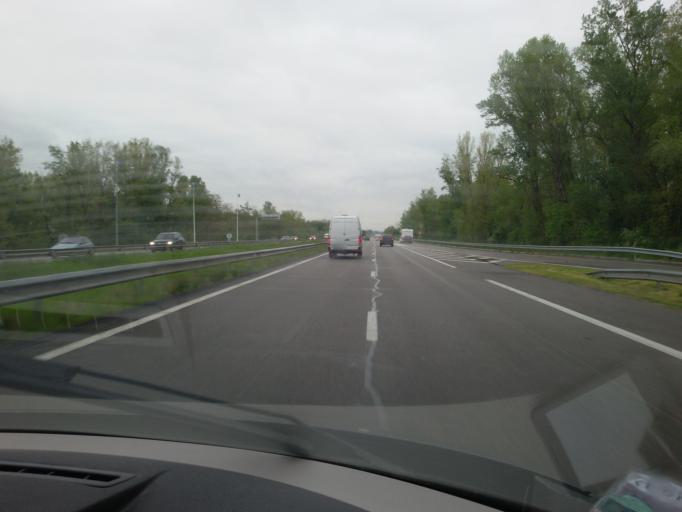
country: FR
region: Rhone-Alpes
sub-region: Departement du Rhone
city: Les Cheres
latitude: 45.9058
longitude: 4.7286
